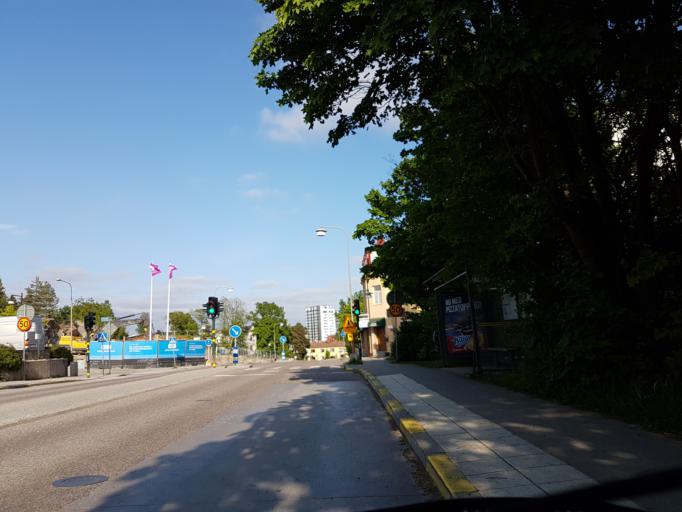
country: SE
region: Stockholm
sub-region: Sundbybergs Kommun
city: Sundbyberg
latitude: 59.3606
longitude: 17.9538
